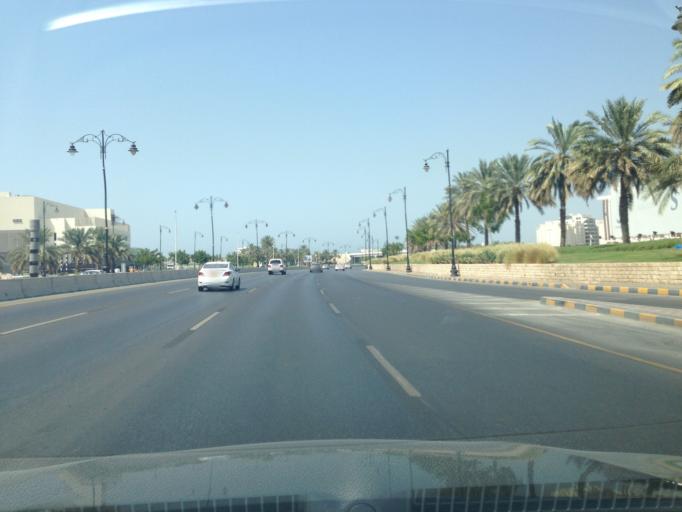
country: OM
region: Muhafazat Masqat
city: Bawshar
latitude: 23.5925
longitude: 58.4095
